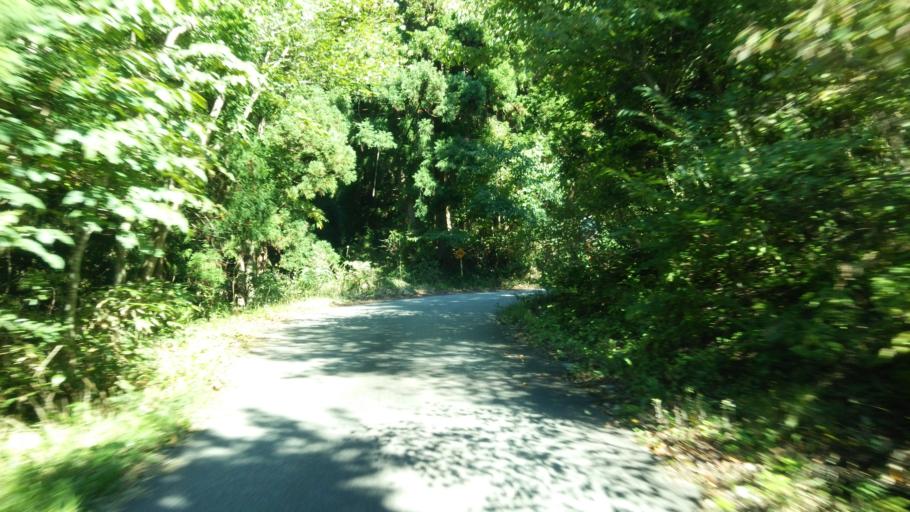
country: JP
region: Fukushima
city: Kitakata
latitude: 37.6238
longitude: 139.9763
